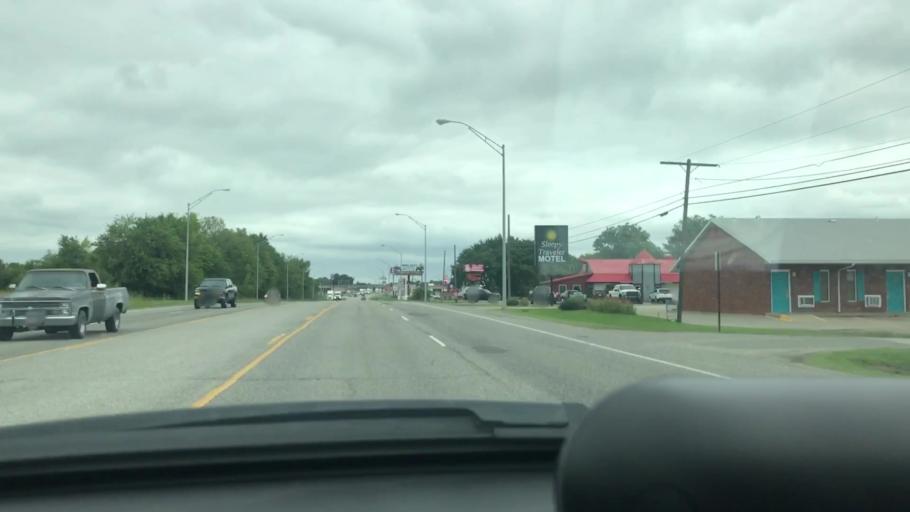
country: US
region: Oklahoma
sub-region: Wagoner County
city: Wagoner
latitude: 35.9522
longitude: -95.3952
